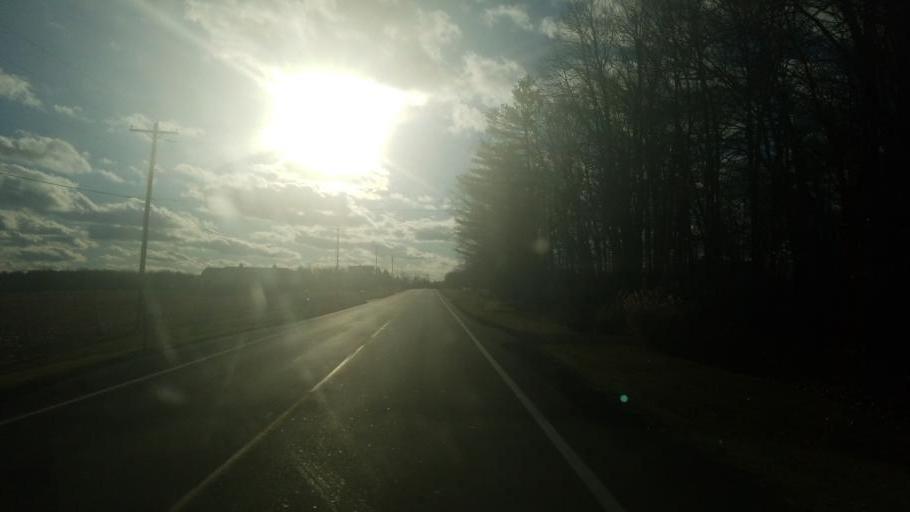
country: US
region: Ohio
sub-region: Richland County
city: Lexington
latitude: 40.6071
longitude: -82.6848
